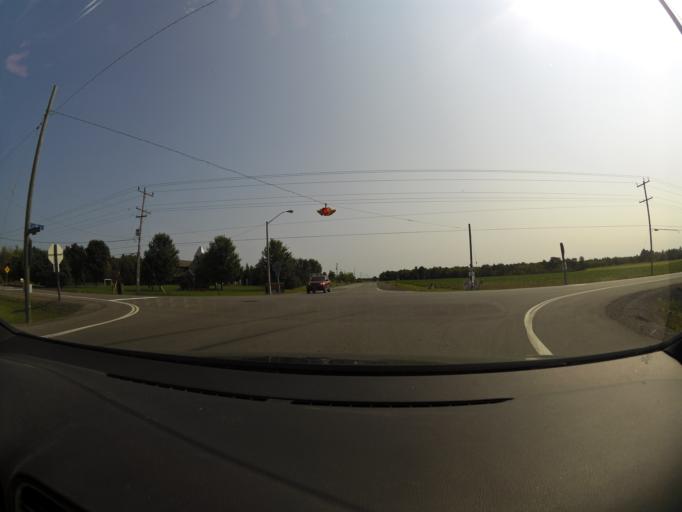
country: CA
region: Ontario
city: Arnprior
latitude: 45.4163
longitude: -76.1494
